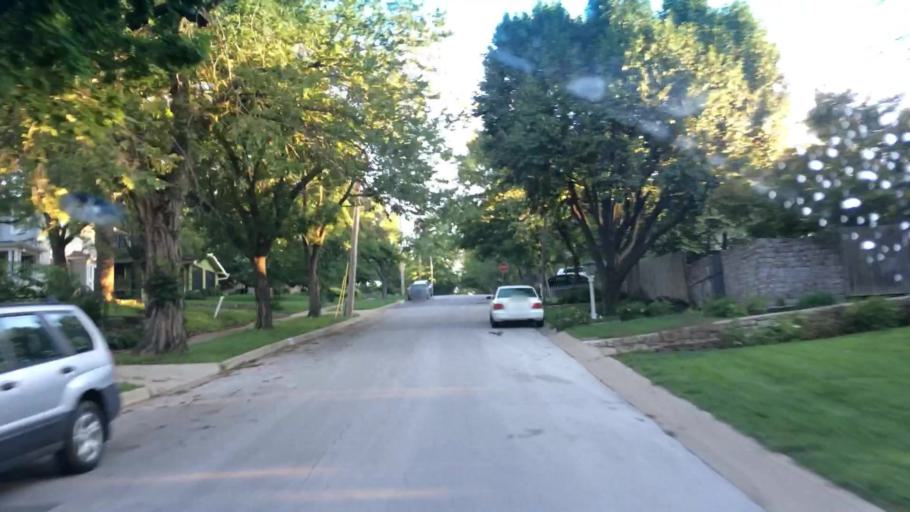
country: US
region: Kansas
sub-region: Johnson County
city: Westwood
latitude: 39.0366
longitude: -94.6057
